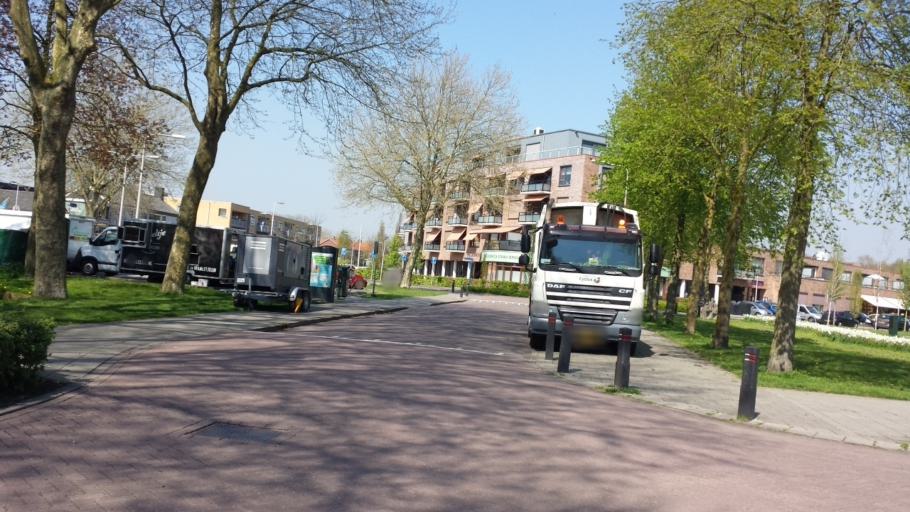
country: NL
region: South Holland
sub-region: Gemeente Vlist
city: Haastrecht
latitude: 51.9743
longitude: 4.7736
